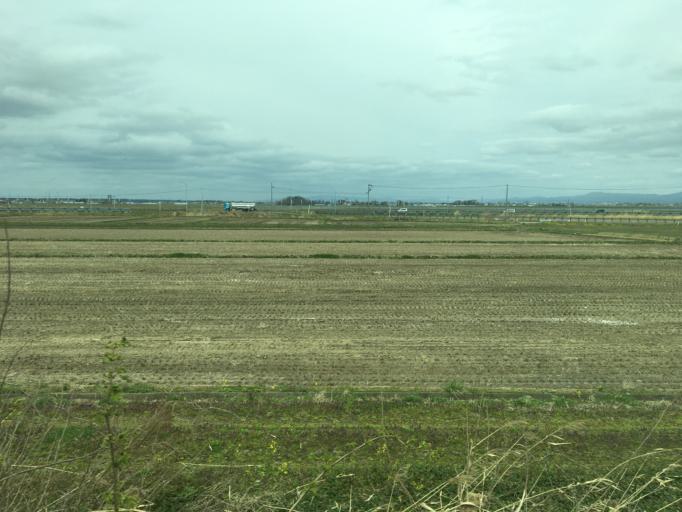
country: JP
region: Aomori
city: Shimokizukuri
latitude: 40.7814
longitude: 140.3424
